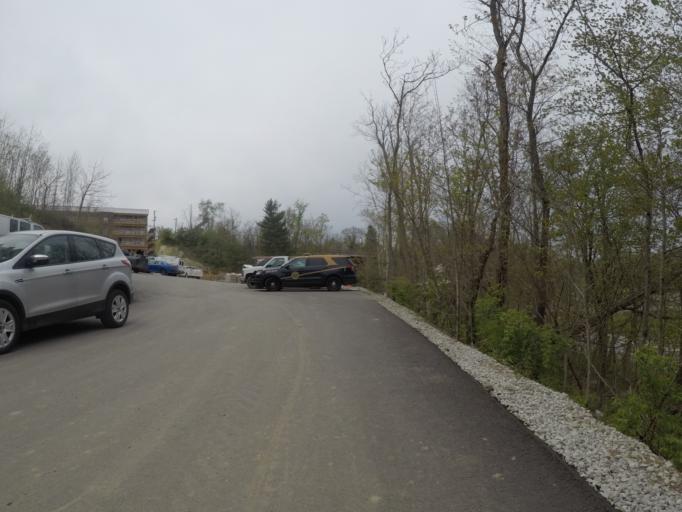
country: US
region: West Virginia
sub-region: Cabell County
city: Pea Ridge
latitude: 38.4114
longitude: -82.3479
